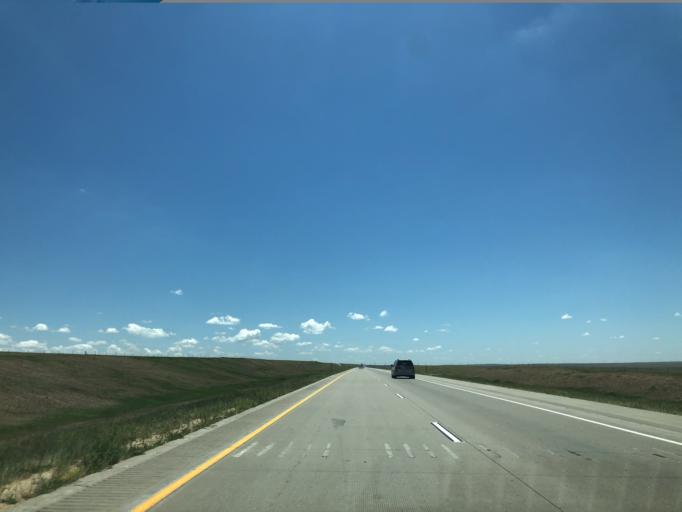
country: US
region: Colorado
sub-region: Lincoln County
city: Limon
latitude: 39.3928
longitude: -103.8950
